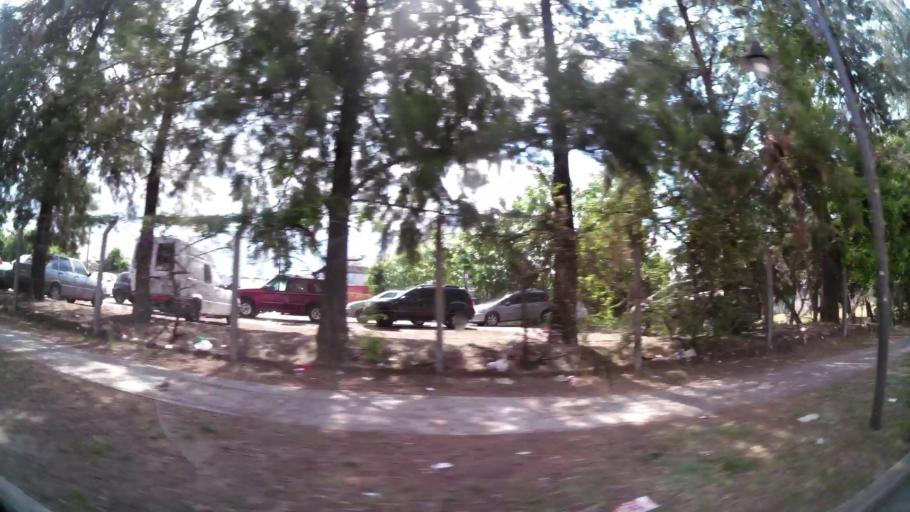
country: AR
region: Buenos Aires
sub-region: Partido de Tigre
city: Tigre
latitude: -34.4701
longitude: -58.5768
